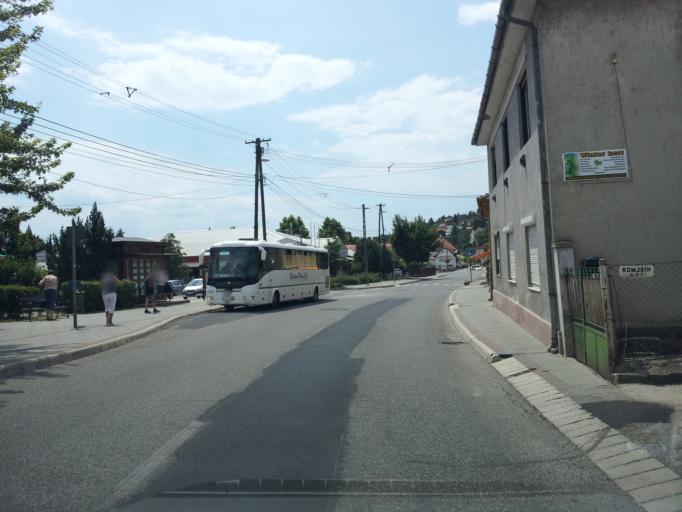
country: HU
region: Veszprem
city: Balatonalmadi
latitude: 47.0333
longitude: 18.0138
